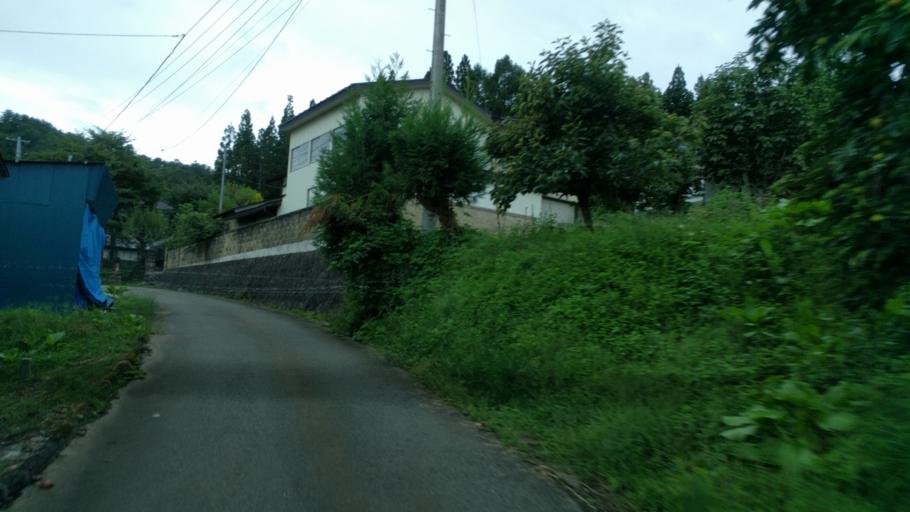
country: JP
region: Fukushima
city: Kitakata
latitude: 37.5419
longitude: 139.7312
